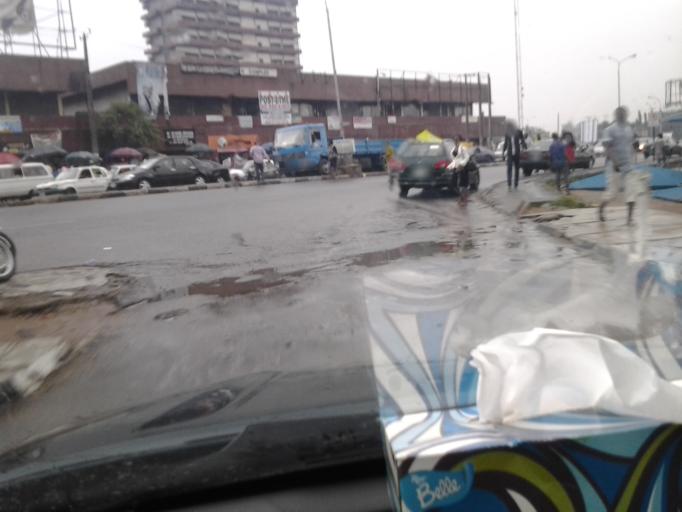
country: NG
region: Oyo
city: Ibadan
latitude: 7.4407
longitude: 3.9066
